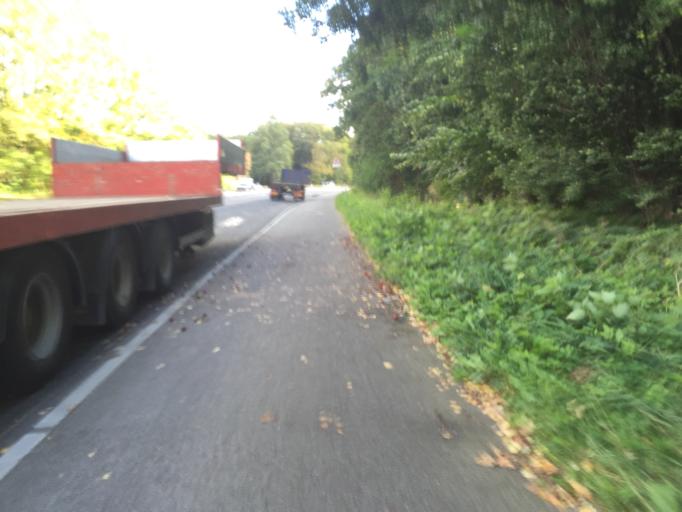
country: DK
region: Capital Region
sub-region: Fureso Kommune
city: Stavnsholt
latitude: 55.7727
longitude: 12.4230
